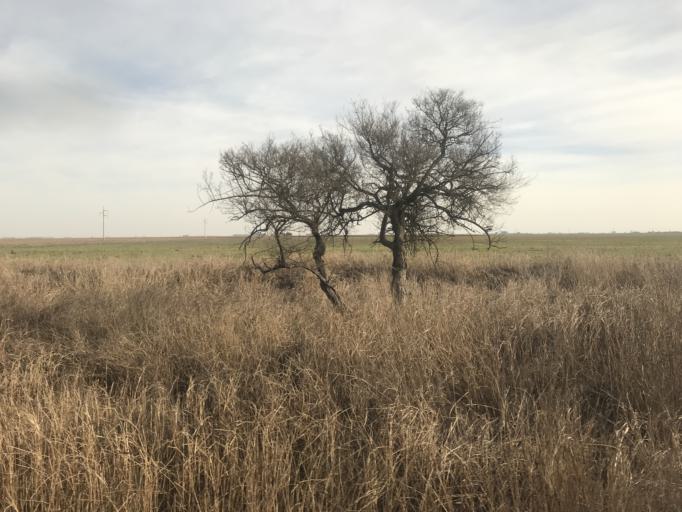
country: AR
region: Cordoba
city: Pilar
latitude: -31.6982
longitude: -63.8718
